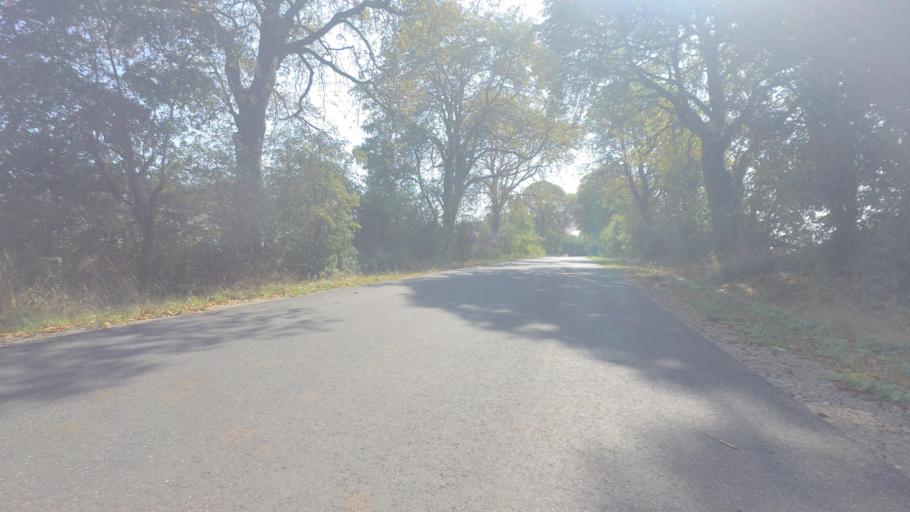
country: DE
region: Mecklenburg-Vorpommern
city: Gielow
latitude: 53.7156
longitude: 12.6904
